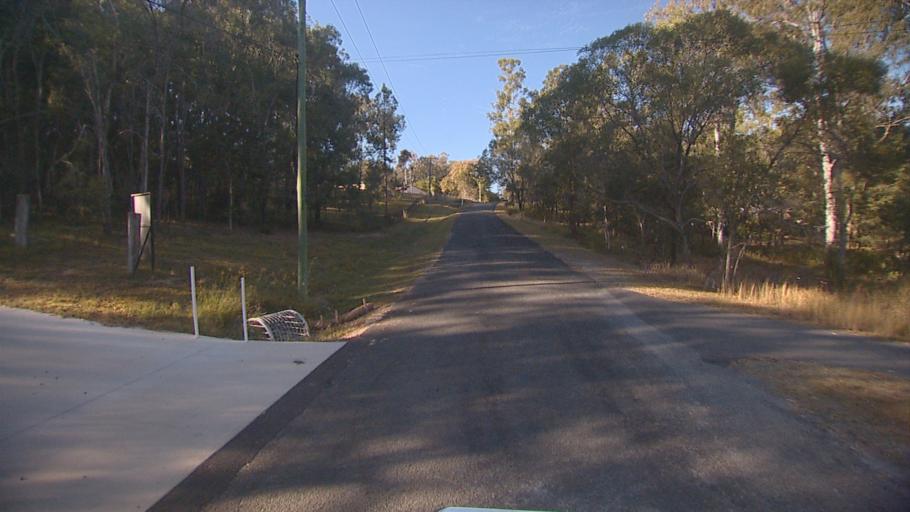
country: AU
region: Queensland
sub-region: Logan
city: Cedar Vale
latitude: -27.8352
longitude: 153.0921
